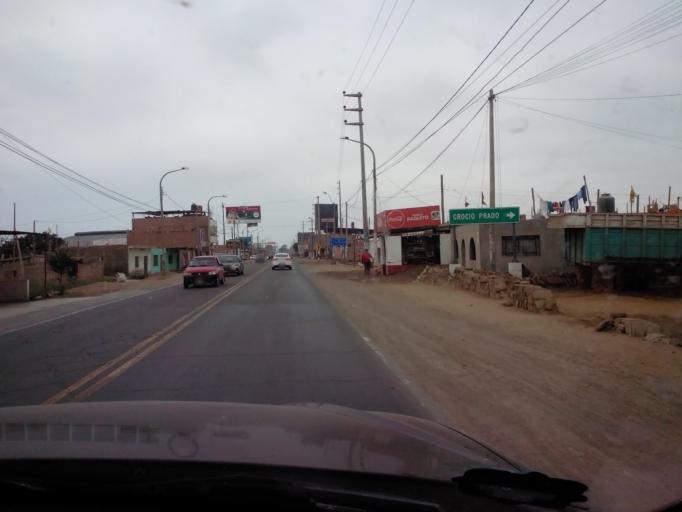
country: PE
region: Ica
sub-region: Provincia de Chincha
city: San Pedro
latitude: -13.4114
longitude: -76.1593
